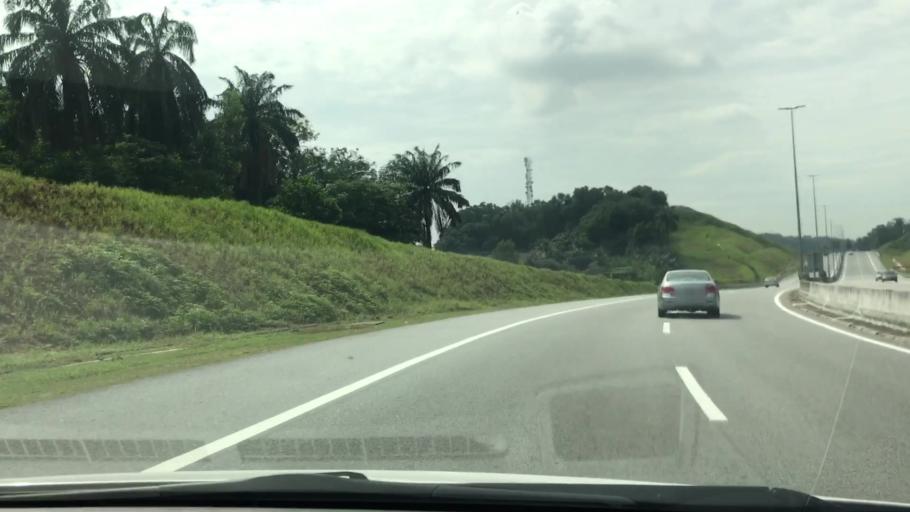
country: MY
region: Selangor
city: Kampong Baharu Balakong
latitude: 3.0109
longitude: 101.6875
